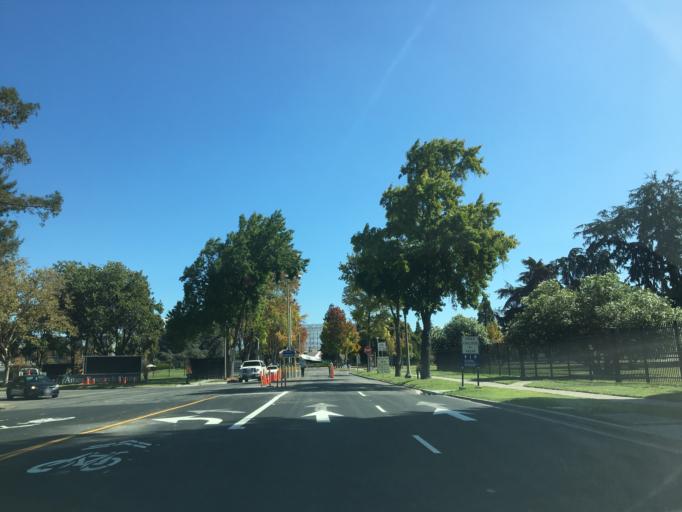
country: US
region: California
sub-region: Santa Clara County
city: Mountain View
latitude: 37.4099
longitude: -122.0633
